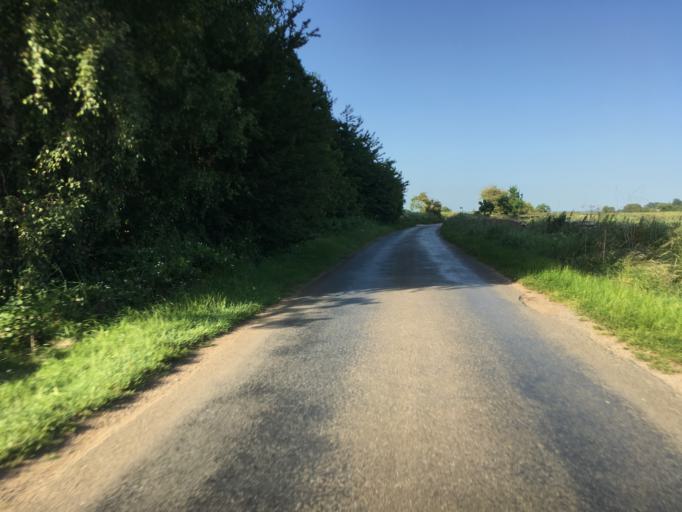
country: GB
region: England
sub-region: Oxfordshire
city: Burford
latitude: 51.7734
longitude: -1.7049
